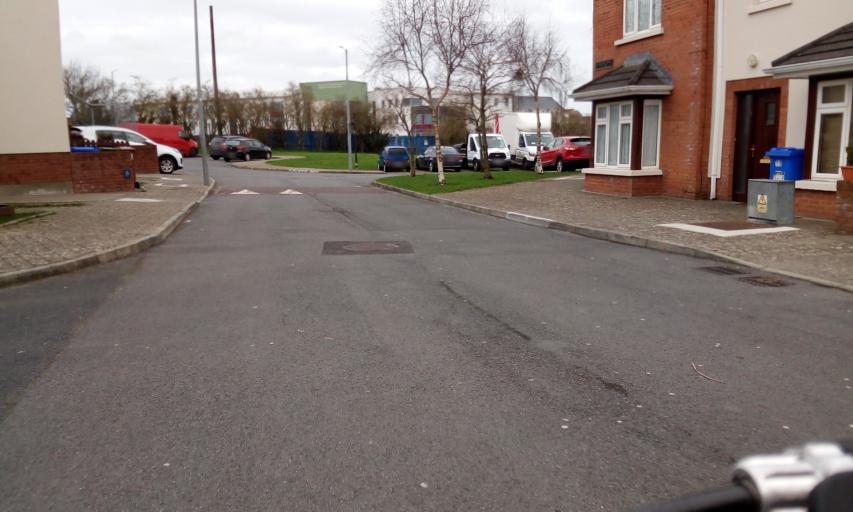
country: IE
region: Leinster
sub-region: Kilkenny
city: Kilkenny
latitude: 52.6579
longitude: -7.2412
